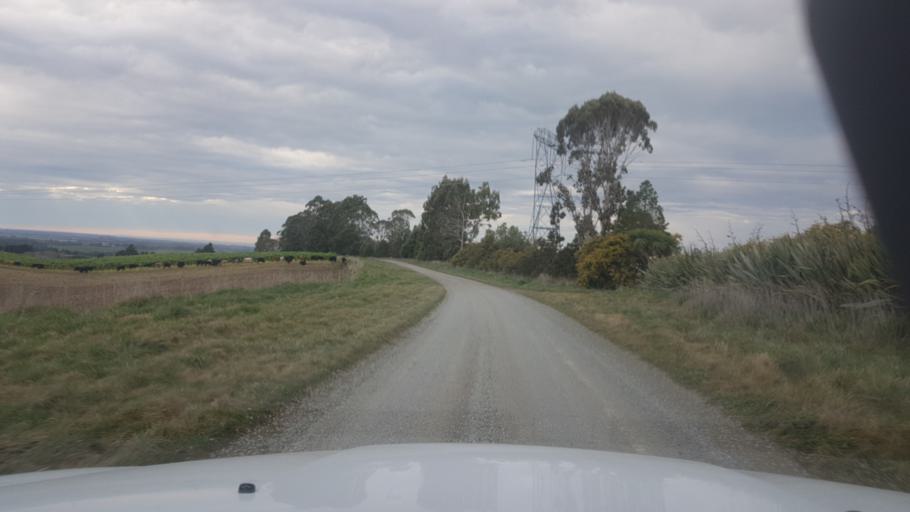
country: NZ
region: Canterbury
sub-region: Timaru District
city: Pleasant Point
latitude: -44.3457
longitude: 171.1321
